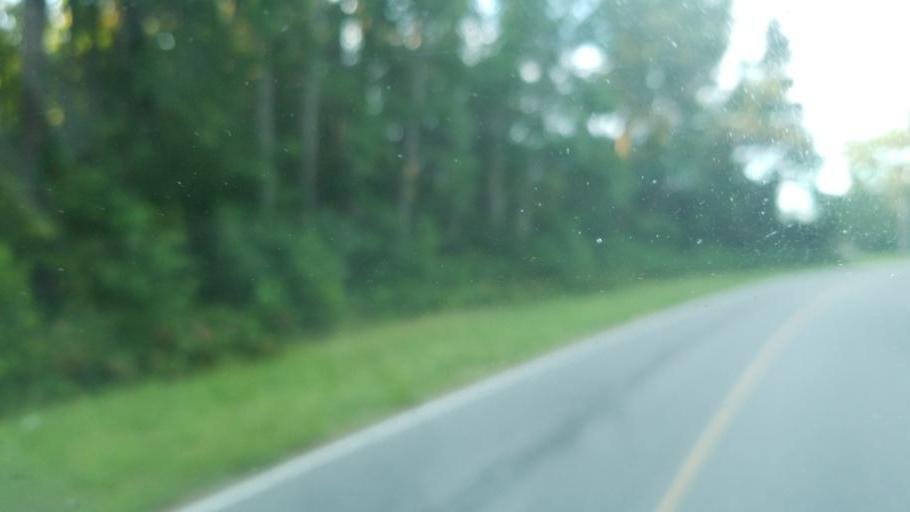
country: US
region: North Carolina
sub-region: Dare County
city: Wanchese
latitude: 35.8433
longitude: -75.6426
